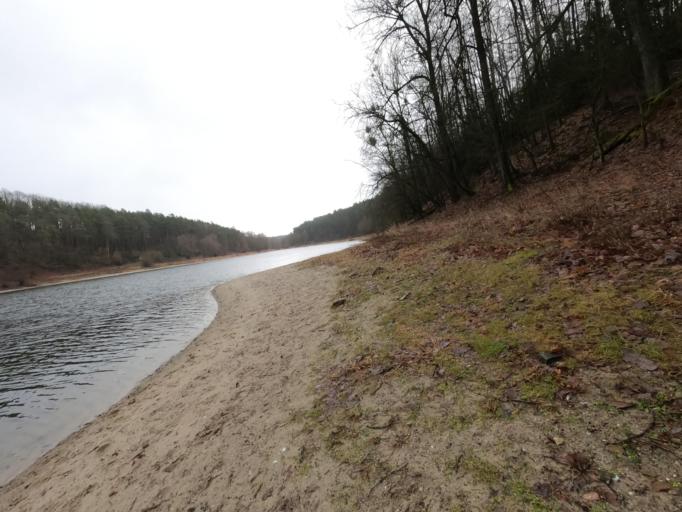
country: PL
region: Greater Poland Voivodeship
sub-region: Powiat pilski
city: Kaczory
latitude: 53.1113
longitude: 16.9045
